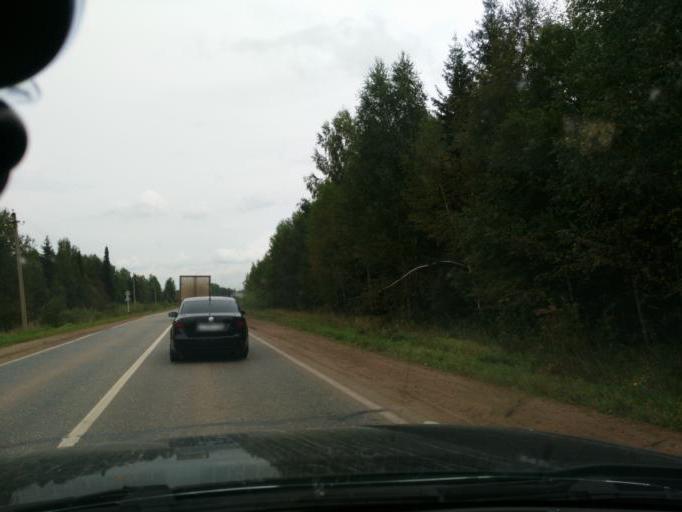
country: RU
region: Bashkortostan
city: Verkhniye Tatyshly
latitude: 56.4966
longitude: 55.8297
